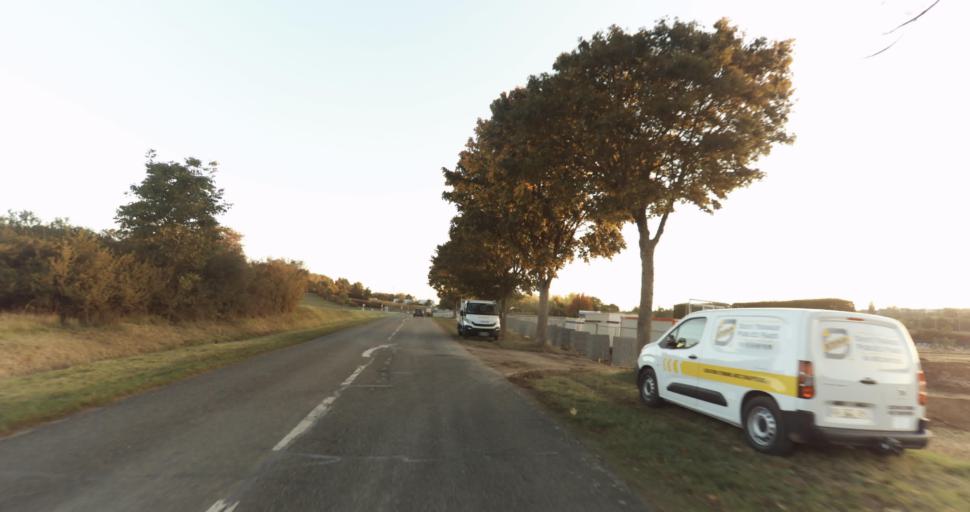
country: FR
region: Centre
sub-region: Departement d'Eure-et-Loir
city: Garnay
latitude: 48.7172
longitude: 1.3463
